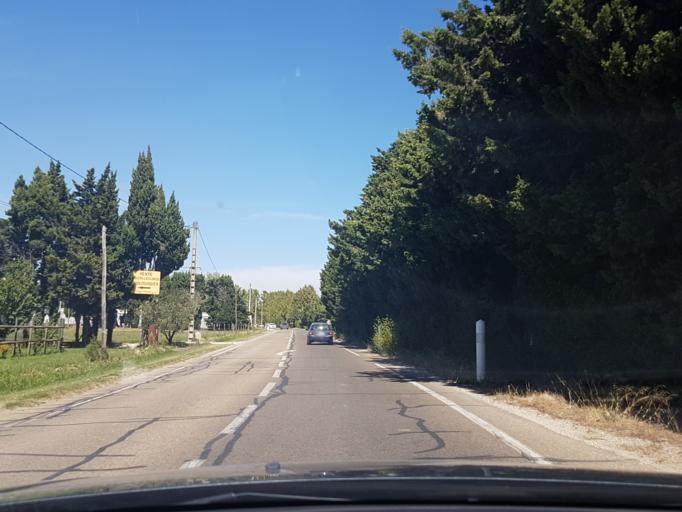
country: FR
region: Provence-Alpes-Cote d'Azur
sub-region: Departement des Bouches-du-Rhone
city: Eyragues
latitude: 43.8570
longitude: 4.8419
